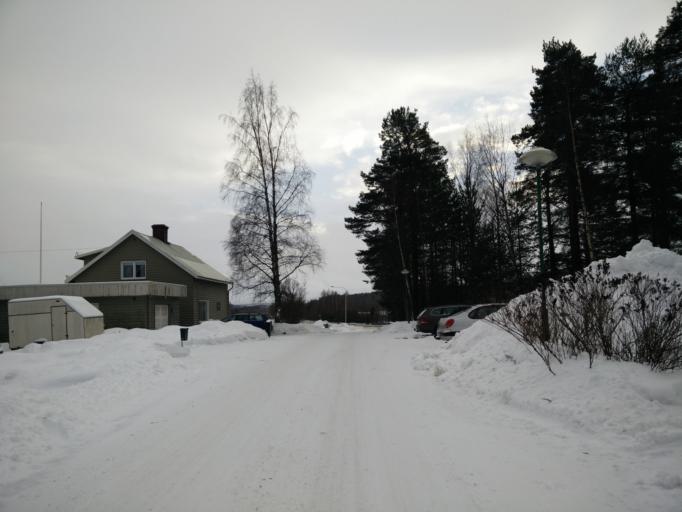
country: SE
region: Vaesternorrland
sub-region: Sundsvalls Kommun
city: Kvissleby
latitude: 62.2901
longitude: 17.3745
